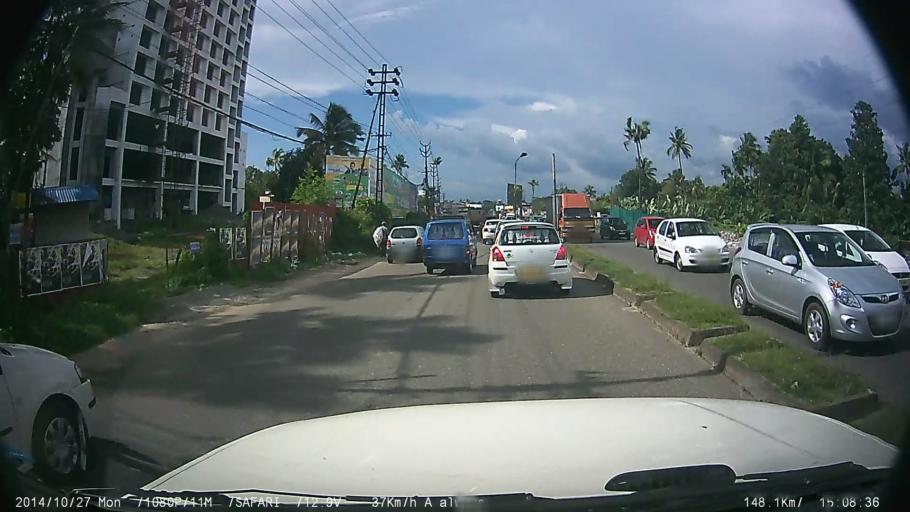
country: IN
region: Kerala
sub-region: Ernakulam
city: Aluva
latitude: 10.1160
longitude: 76.3449
